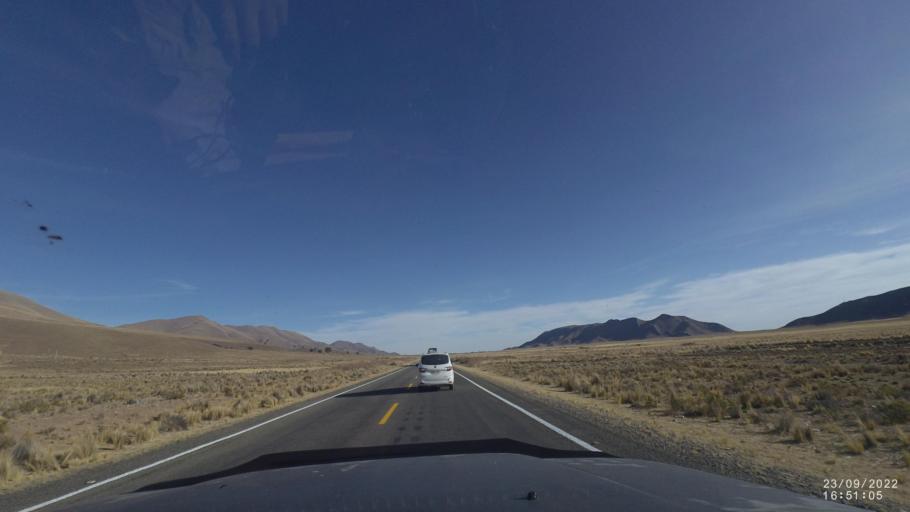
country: BO
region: Oruro
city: Poopo
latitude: -18.4103
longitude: -66.9766
